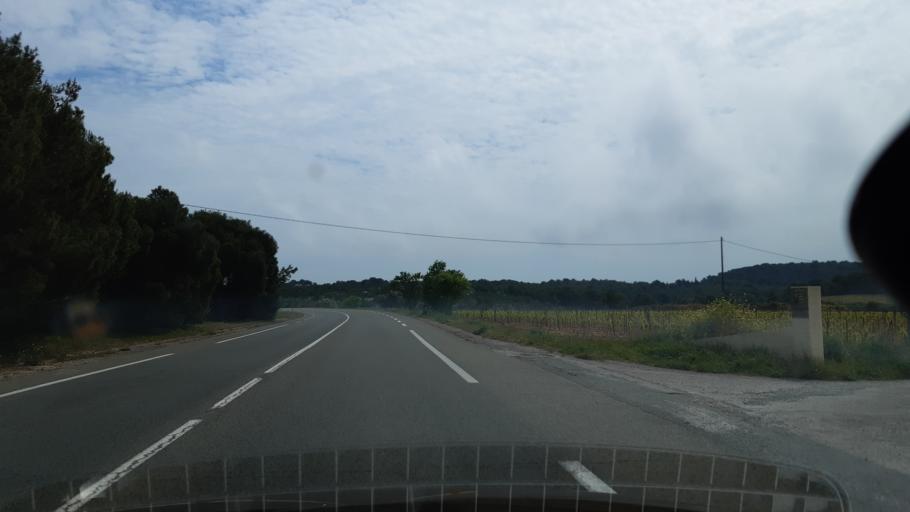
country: FR
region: Languedoc-Roussillon
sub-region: Departement de l'Aude
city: Gruissan
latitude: 43.1261
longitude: 3.0622
